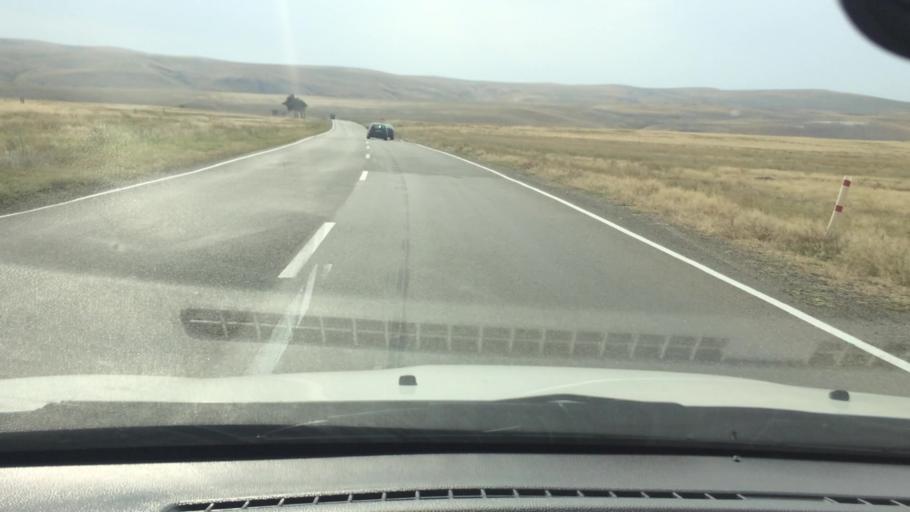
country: GE
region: Kvemo Kartli
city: Rust'avi
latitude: 41.5326
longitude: 44.9435
